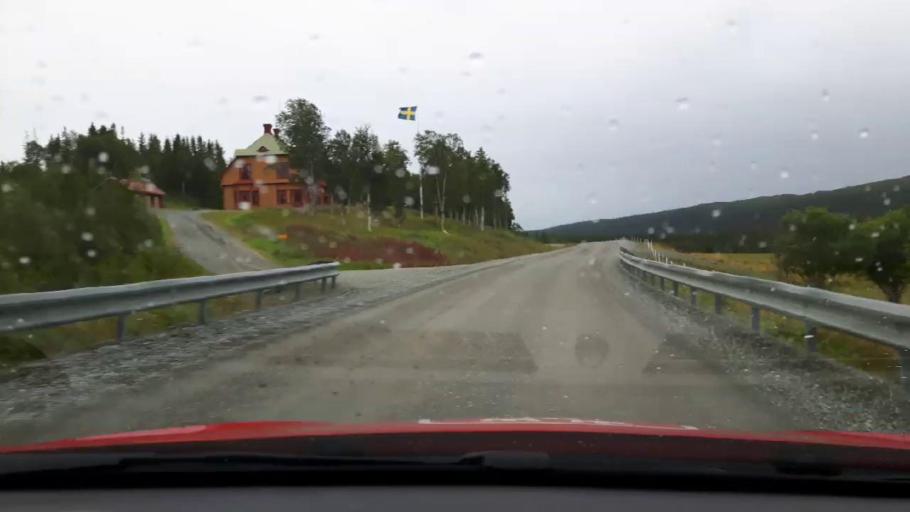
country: NO
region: Nord-Trondelag
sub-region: Meraker
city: Meraker
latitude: 63.5215
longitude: 12.4052
